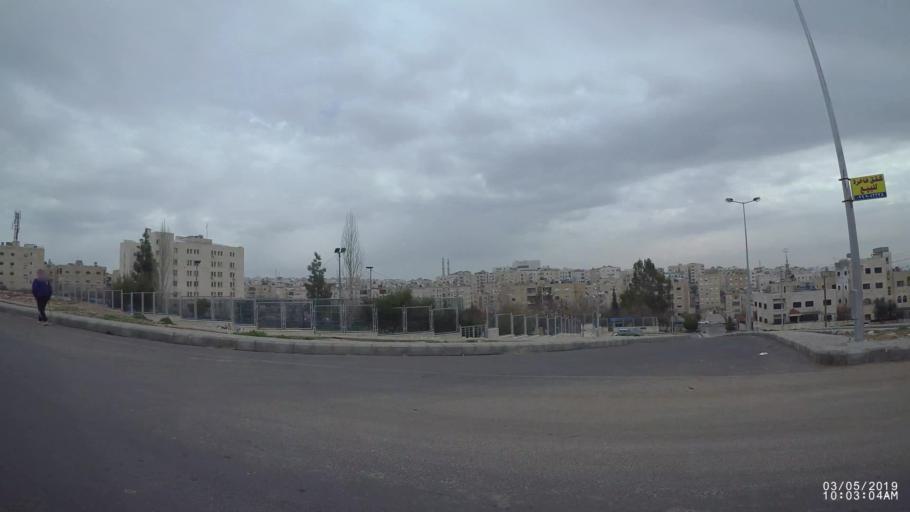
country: JO
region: Amman
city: Amman
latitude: 31.9814
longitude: 35.9312
